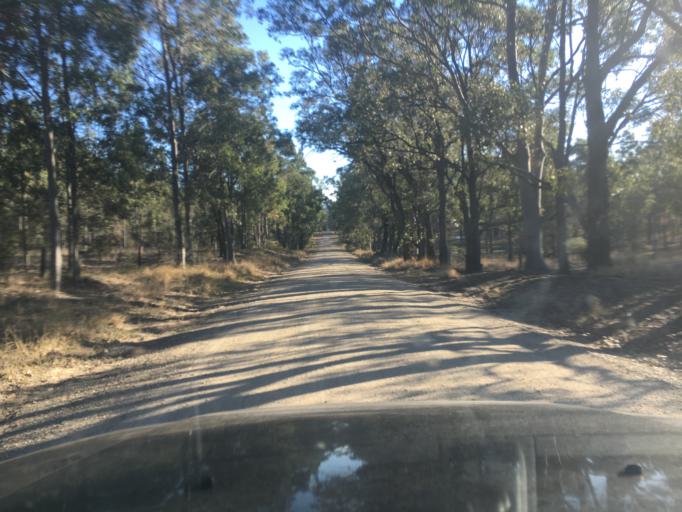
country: AU
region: New South Wales
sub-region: Singleton
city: Singleton
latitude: -32.5533
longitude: 151.2367
